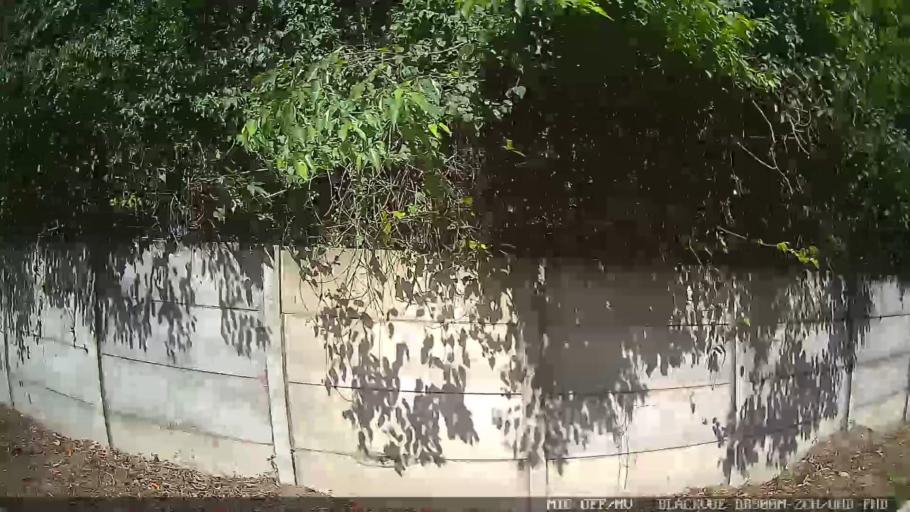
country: BR
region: Sao Paulo
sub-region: Atibaia
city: Atibaia
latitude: -23.1397
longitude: -46.5478
